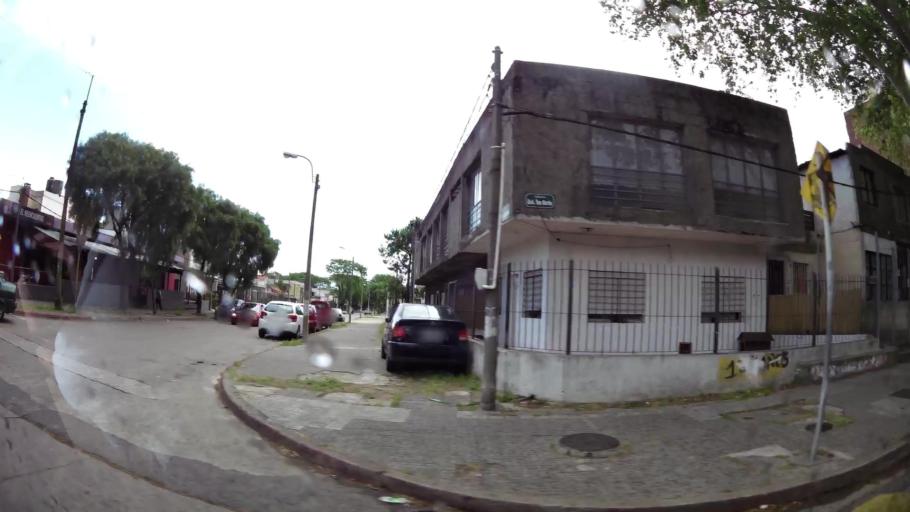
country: UY
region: Montevideo
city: Montevideo
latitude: -34.8606
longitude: -56.1778
